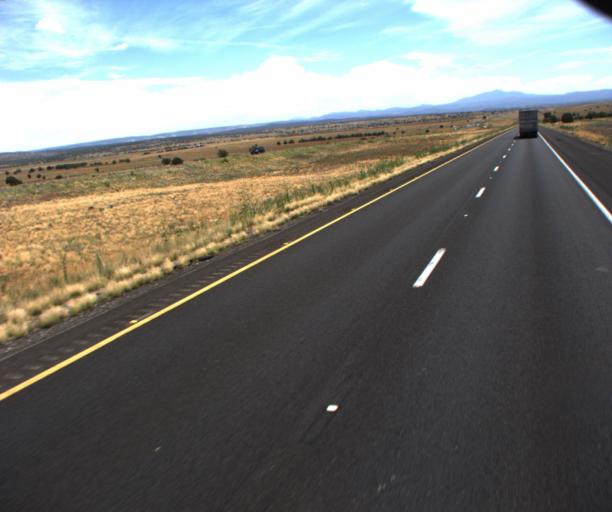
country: US
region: Arizona
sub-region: Yavapai County
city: Paulden
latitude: 35.2331
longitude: -112.6178
